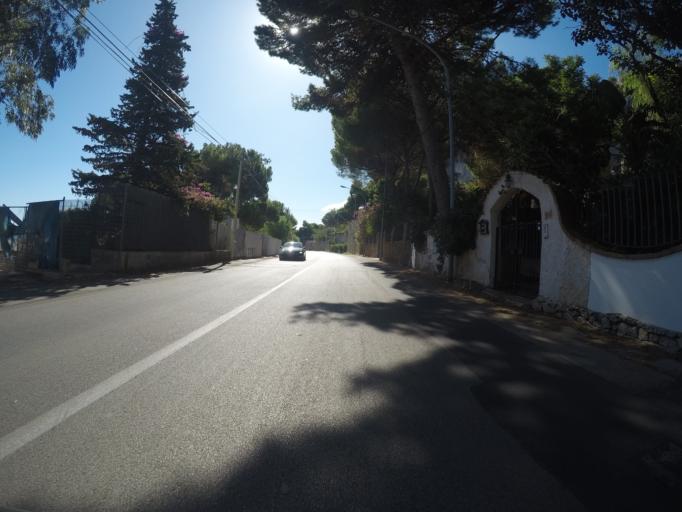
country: IT
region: Sicily
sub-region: Palermo
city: Palermo
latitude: 38.1876
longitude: 13.3601
